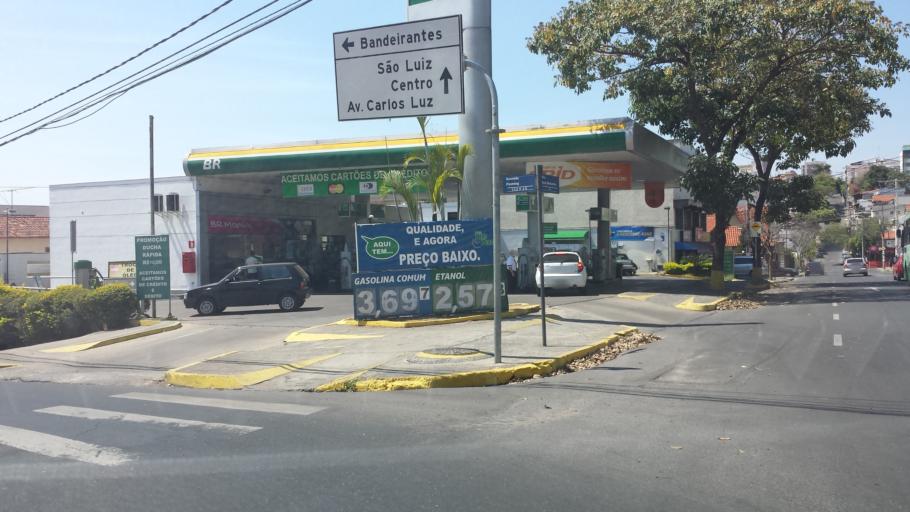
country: BR
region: Minas Gerais
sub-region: Belo Horizonte
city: Belo Horizonte
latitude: -19.8740
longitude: -43.9877
